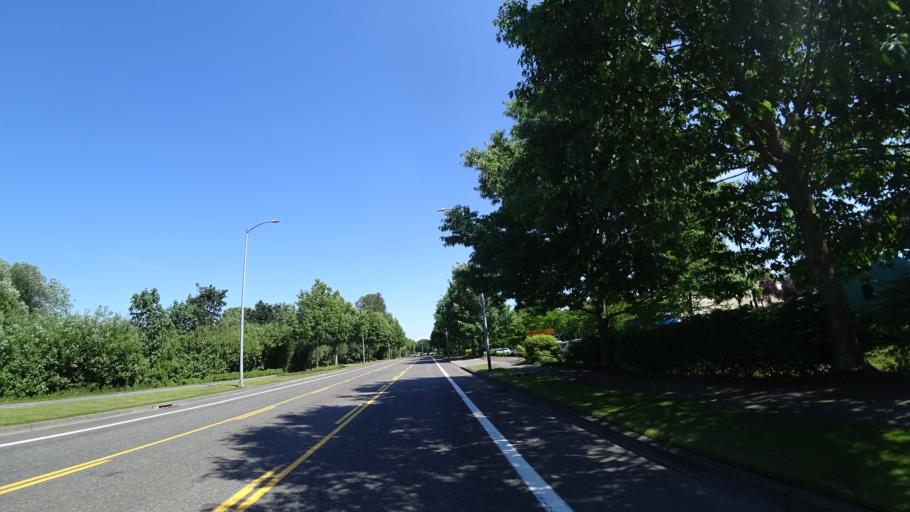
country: US
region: Oregon
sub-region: Multnomah County
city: Lents
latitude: 45.5715
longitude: -122.5726
